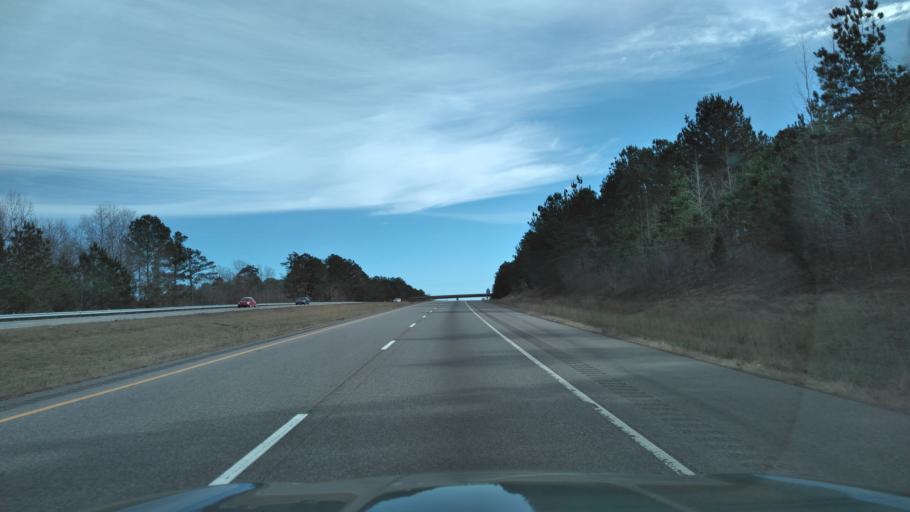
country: US
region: Alabama
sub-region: Marion County
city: Hamilton
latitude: 34.1918
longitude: -88.1135
